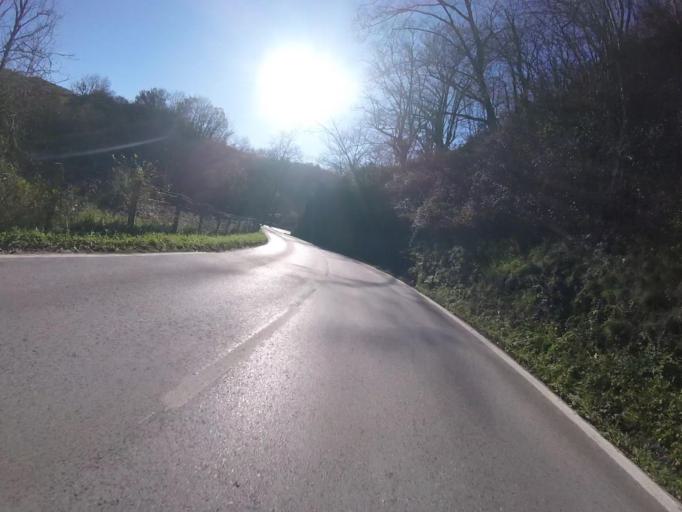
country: ES
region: Navarre
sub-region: Provincia de Navarra
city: Bera
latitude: 43.2833
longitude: -1.6483
